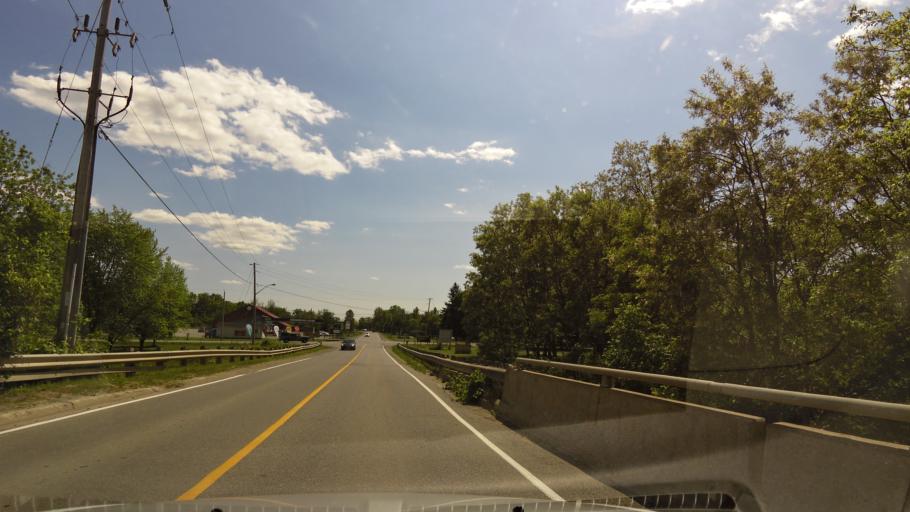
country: CA
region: Ontario
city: Ancaster
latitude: 43.0966
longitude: -80.0992
